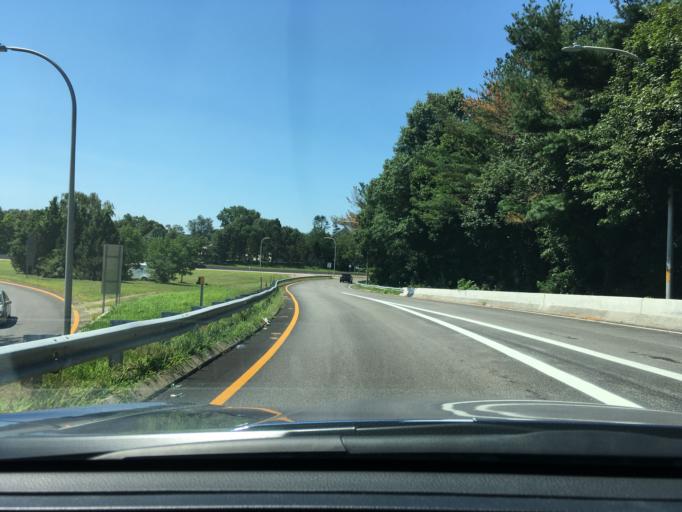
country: US
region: Rhode Island
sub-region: Providence County
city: Cranston
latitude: 41.7830
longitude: -71.4253
